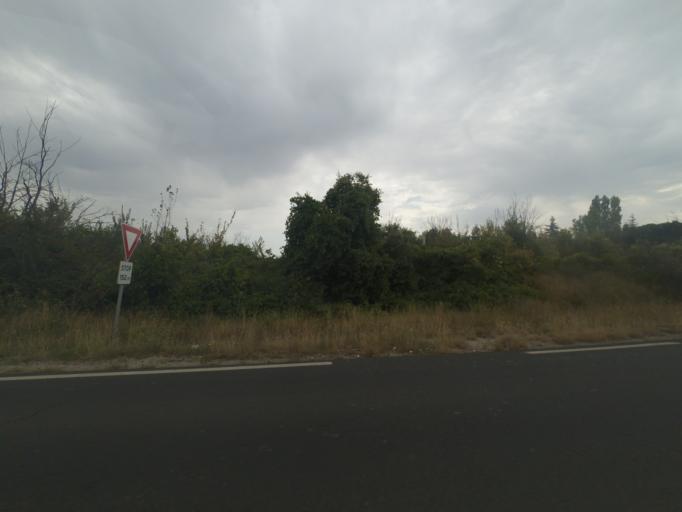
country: FR
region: Languedoc-Roussillon
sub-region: Departement de l'Herault
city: Saint-Mathieu-de-Treviers
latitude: 43.7459
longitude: 3.8582
